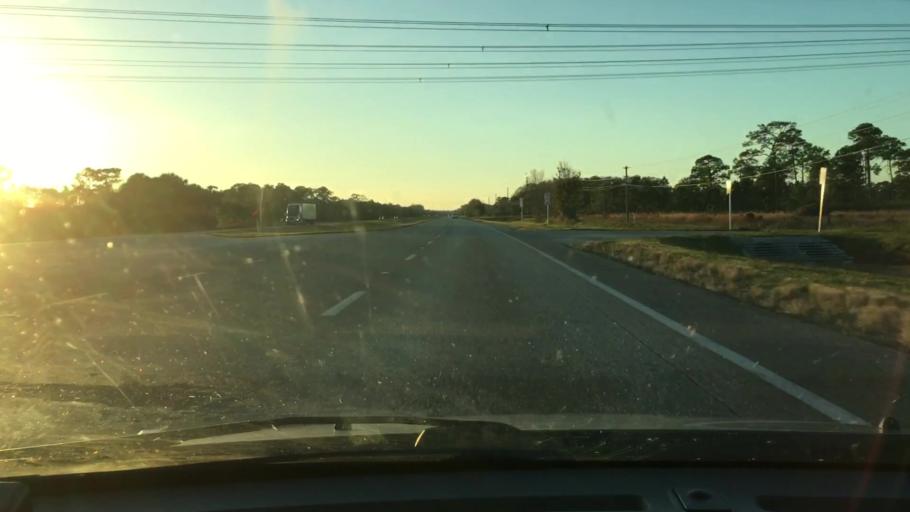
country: US
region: Florida
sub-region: Indian River County
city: Fellsmere
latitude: 27.6812
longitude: -80.8372
